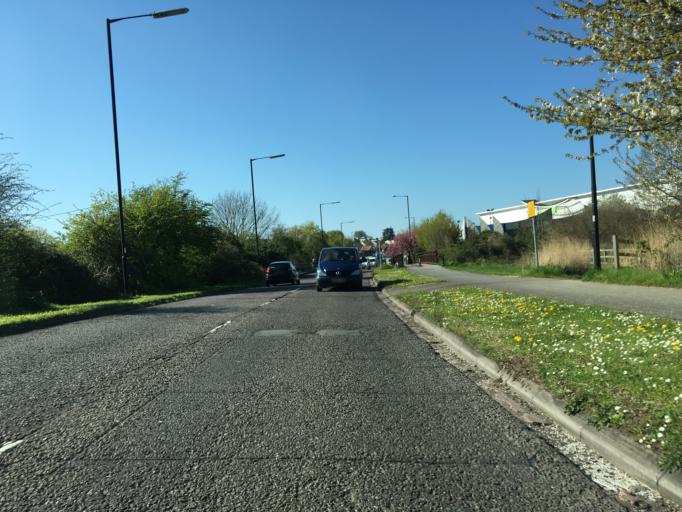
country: GB
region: England
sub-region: North Somerset
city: Portishead
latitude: 51.4823
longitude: -2.7638
